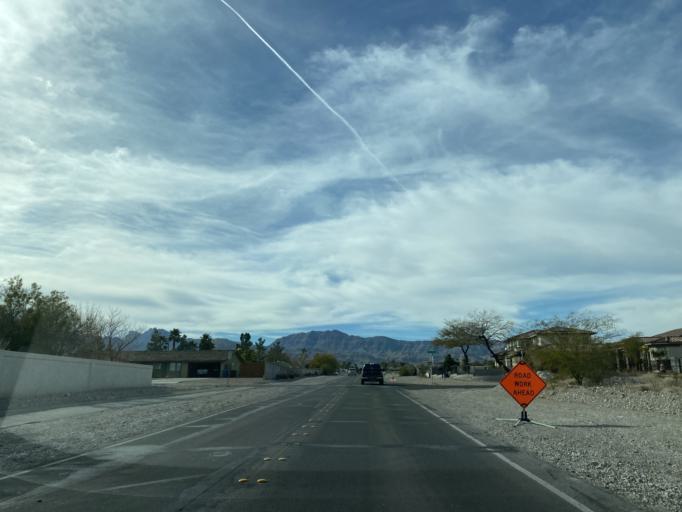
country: US
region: Nevada
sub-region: Clark County
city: Summerlin South
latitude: 36.2700
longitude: -115.2944
